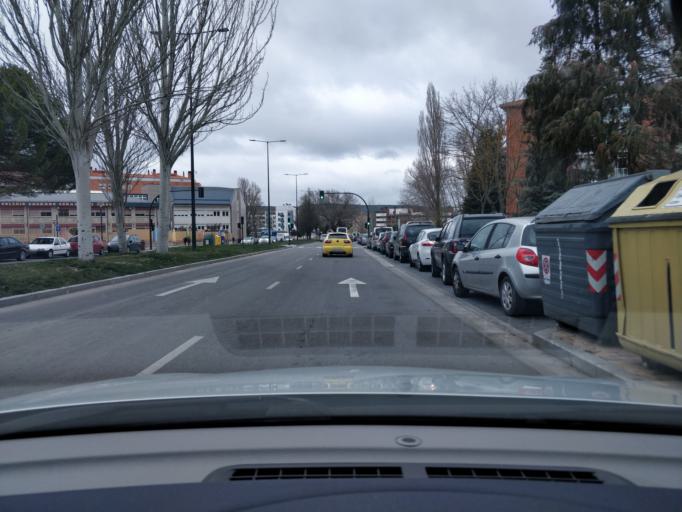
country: ES
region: Castille and Leon
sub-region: Provincia de Burgos
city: Burgos
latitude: 42.3636
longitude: -3.6537
